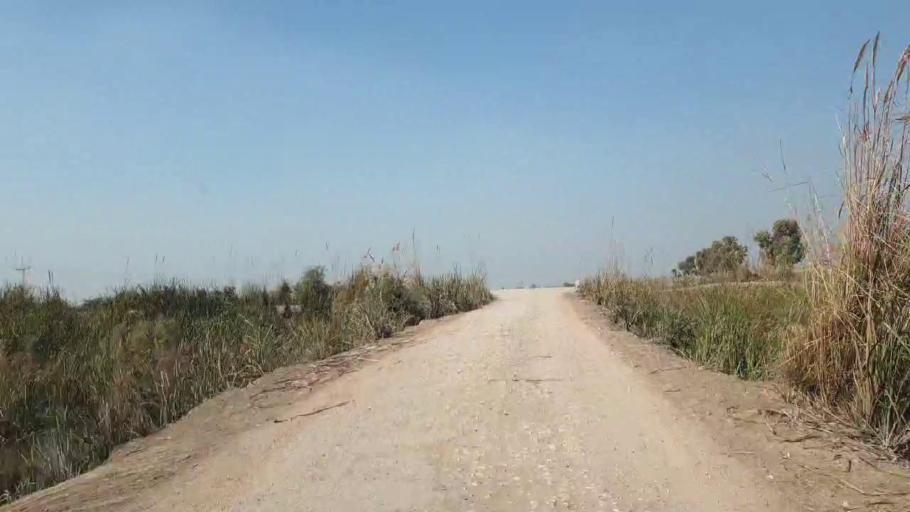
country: PK
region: Sindh
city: Bhit Shah
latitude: 25.9207
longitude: 68.4939
